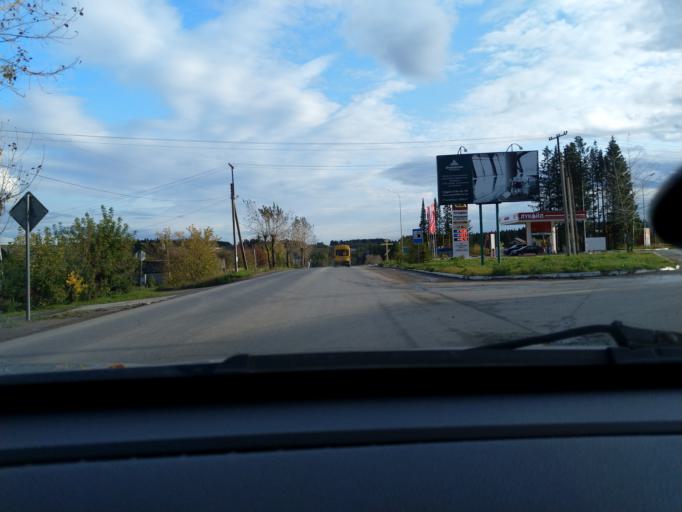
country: RU
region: Perm
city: Polazna
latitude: 58.2836
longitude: 56.4111
